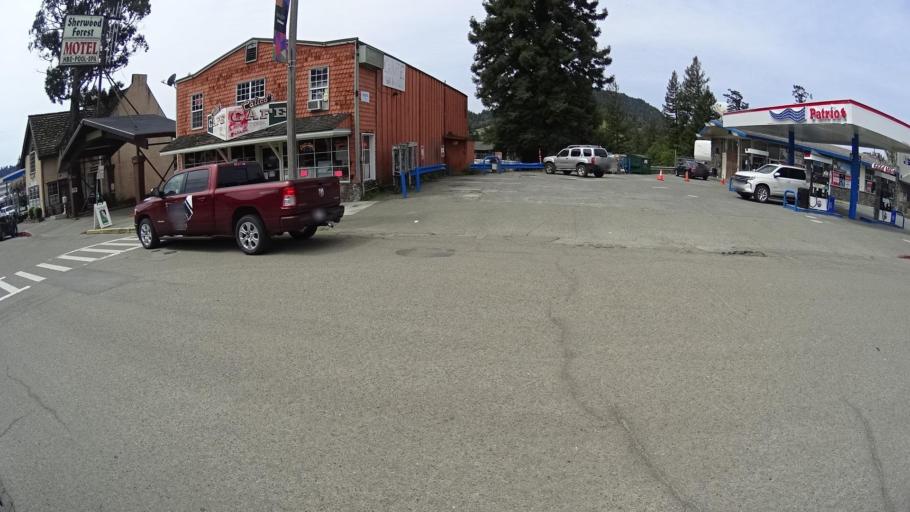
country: US
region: California
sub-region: Humboldt County
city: Redway
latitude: 40.1002
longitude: -123.7950
